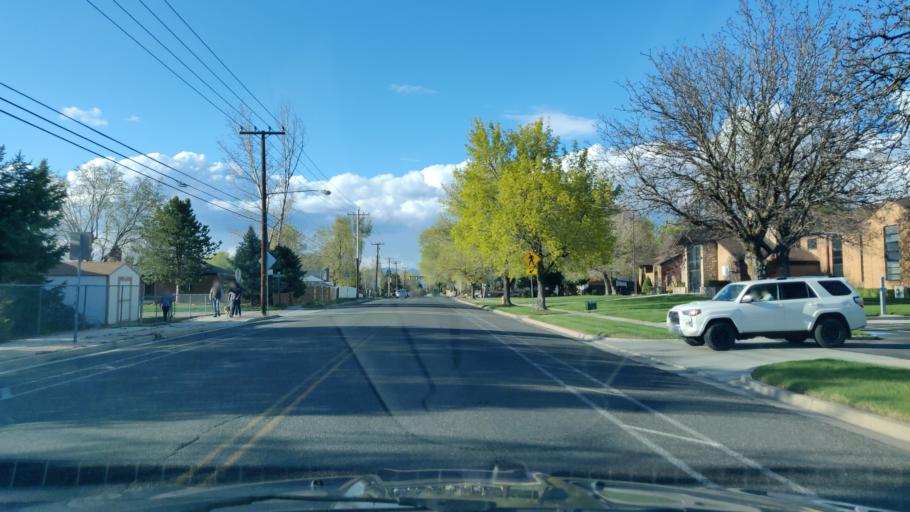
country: US
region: Utah
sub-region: Salt Lake County
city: Cottonwood Heights
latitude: 40.6361
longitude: -111.8247
